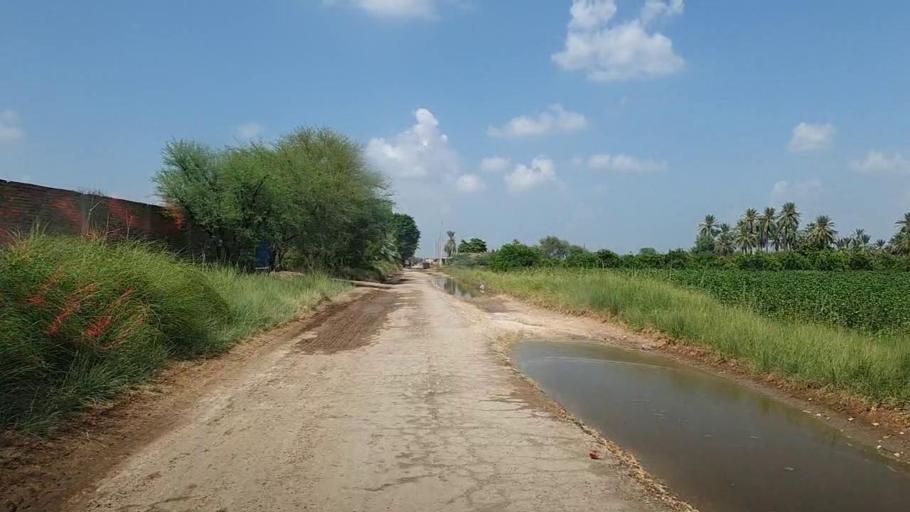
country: PK
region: Sindh
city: Kandiaro
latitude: 27.0262
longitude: 68.2749
